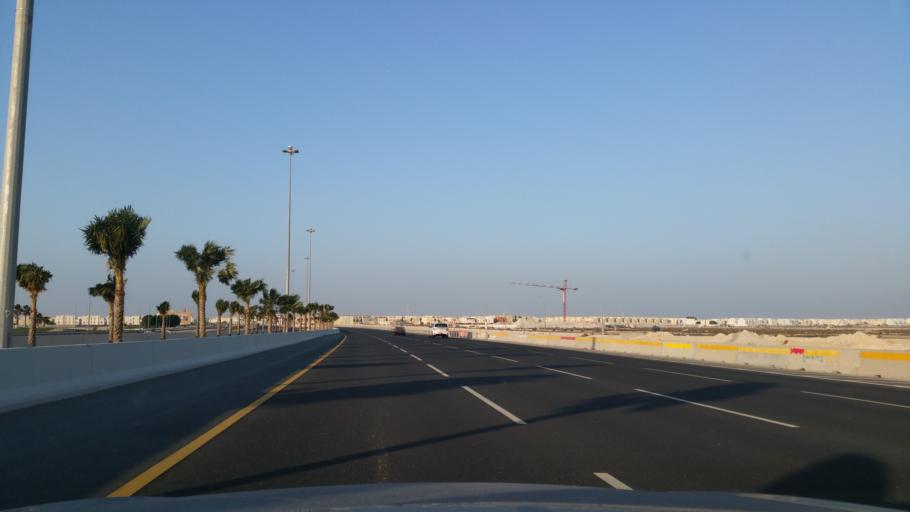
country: QA
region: Al Khawr
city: Al Khawr
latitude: 25.6576
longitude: 51.4998
